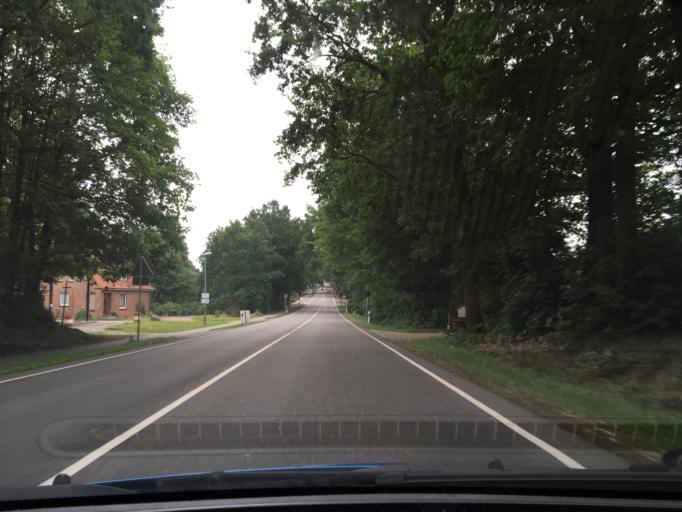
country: DE
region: Lower Saxony
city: Wenzendorf
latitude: 53.3846
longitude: 9.7978
